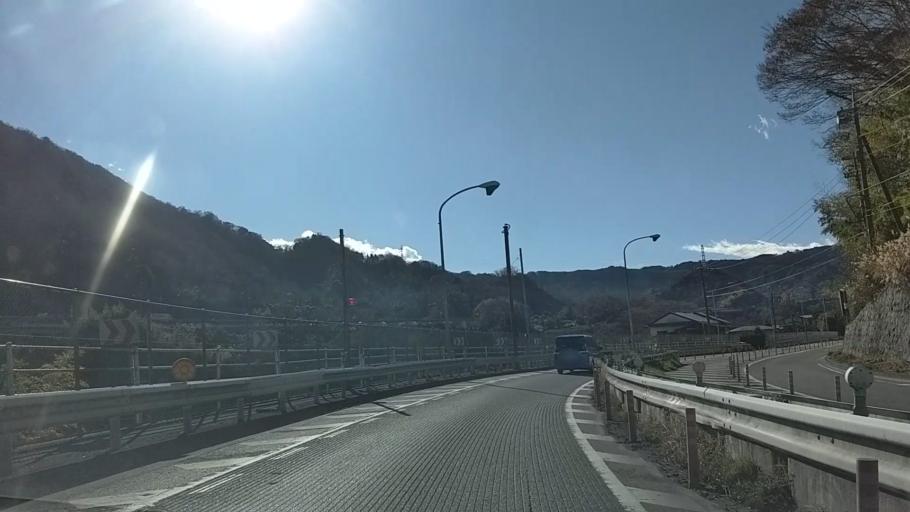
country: JP
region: Shizuoka
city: Gotemba
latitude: 35.3630
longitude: 139.0184
